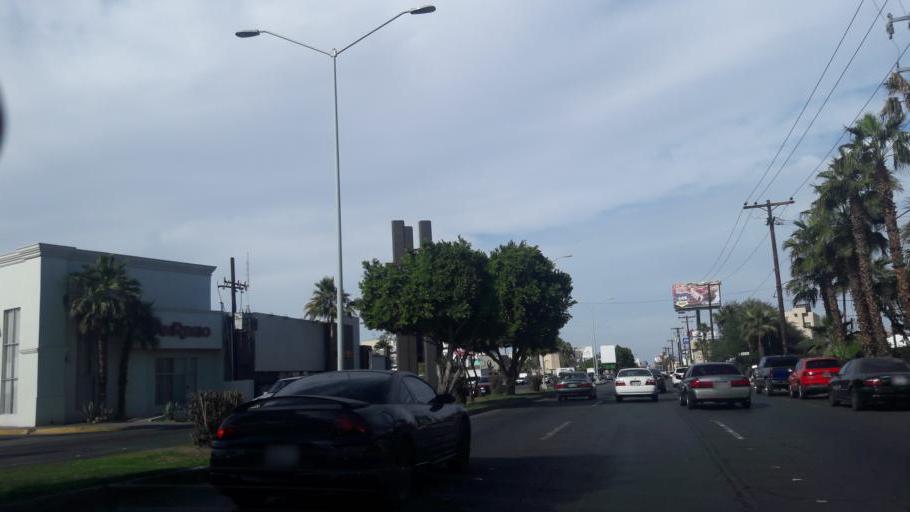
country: MX
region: Baja California
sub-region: Mexicali
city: Mexicali
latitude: 32.6407
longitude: -115.4497
